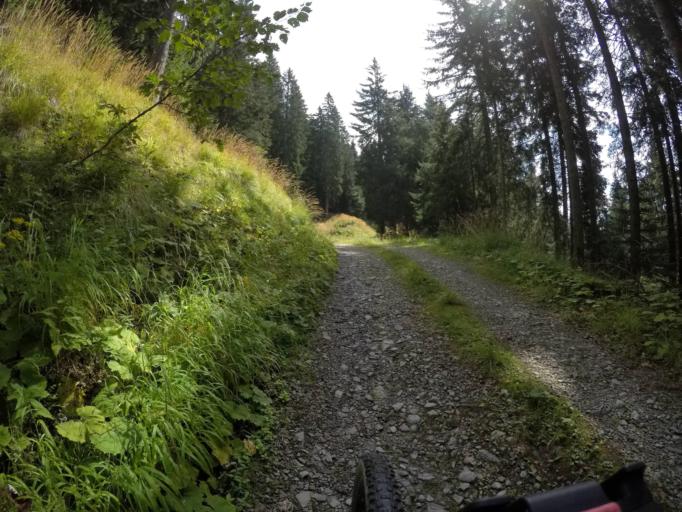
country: IT
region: Friuli Venezia Giulia
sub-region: Provincia di Udine
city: Paularo
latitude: 46.5123
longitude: 13.2029
